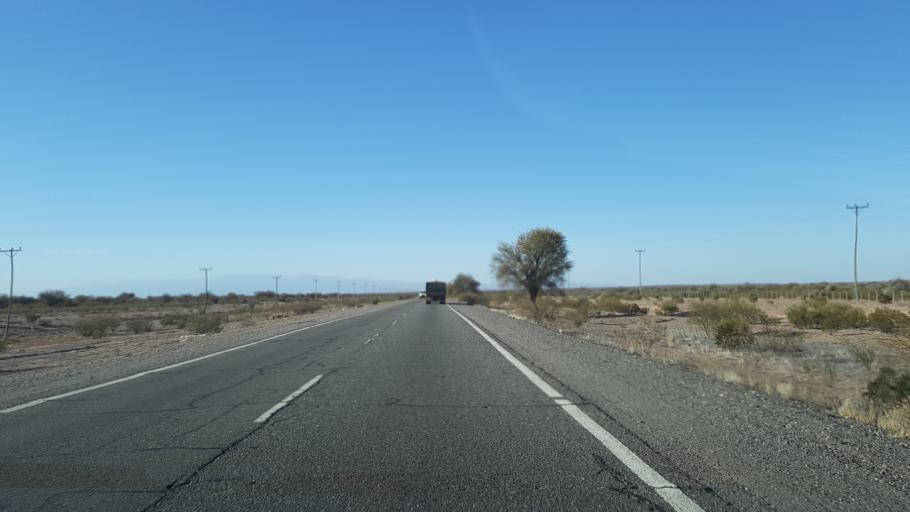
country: AR
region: San Juan
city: Caucete
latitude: -31.6565
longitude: -67.7715
